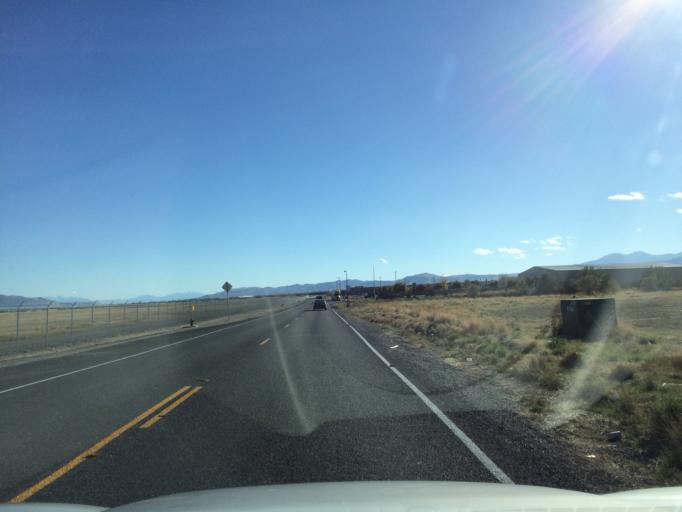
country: US
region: Utah
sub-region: Salt Lake County
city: Kearns
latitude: 40.6371
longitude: -111.9998
